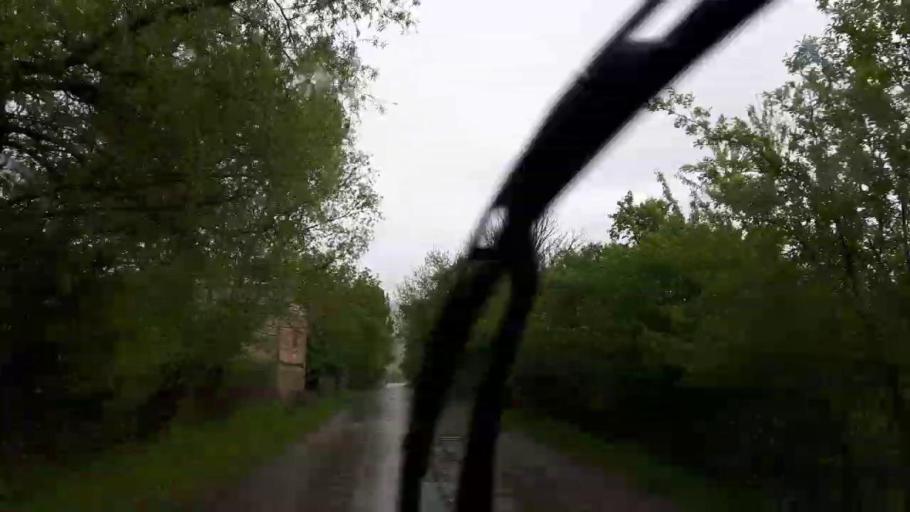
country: GE
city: Agara
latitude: 42.0047
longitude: 43.7604
